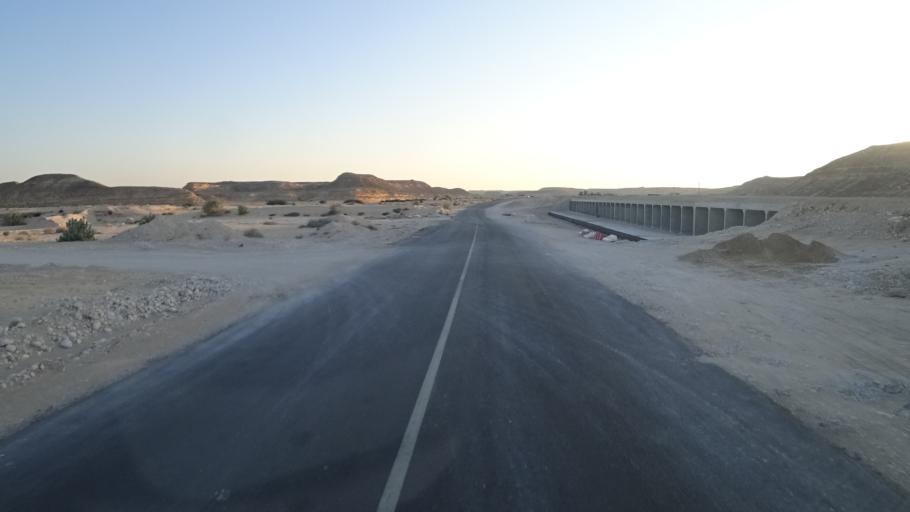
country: OM
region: Zufar
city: Salalah
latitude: 17.5180
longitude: 53.3753
